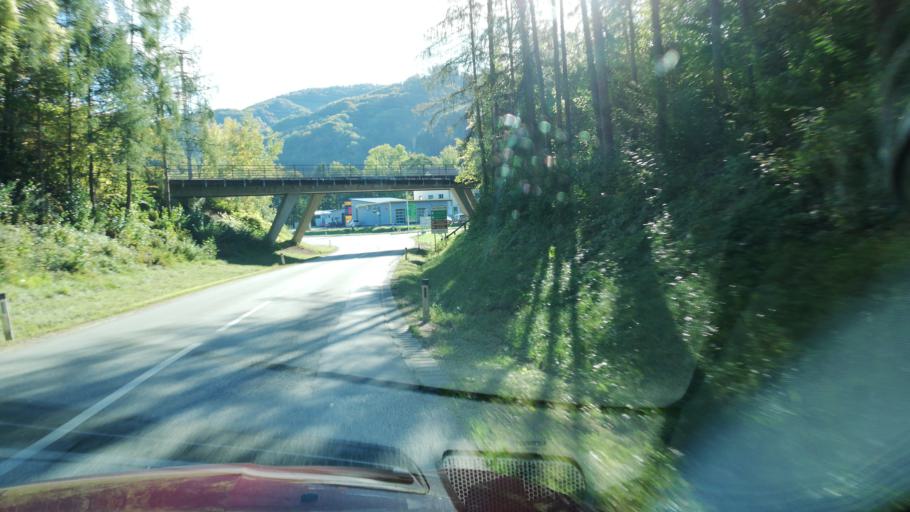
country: AT
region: Upper Austria
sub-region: Politischer Bezirk Steyr-Land
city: Ternberg
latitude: 47.9543
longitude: 14.3545
